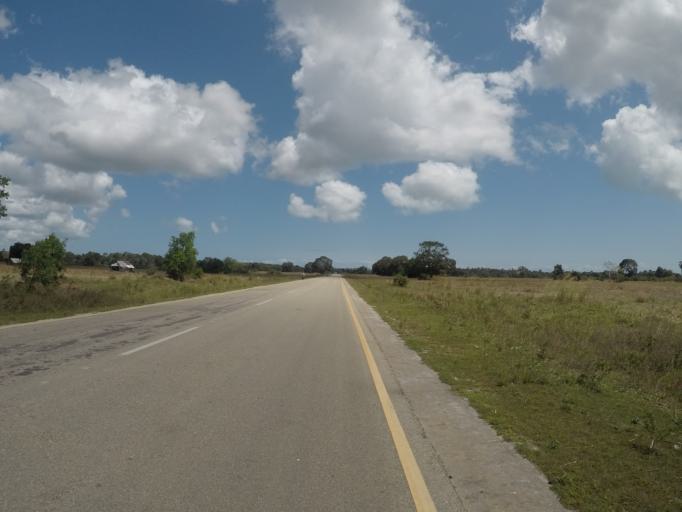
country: TZ
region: Zanzibar Central/South
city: Koani
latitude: -6.2204
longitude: 39.3629
